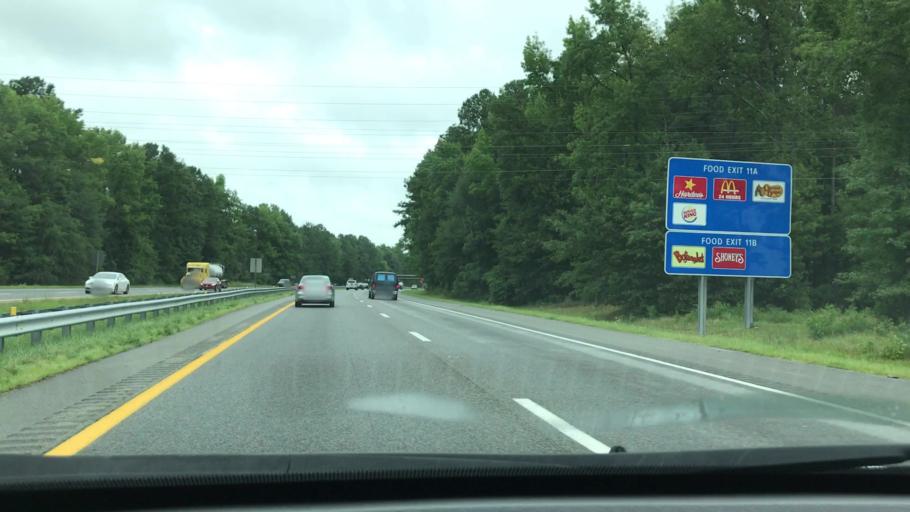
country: US
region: Virginia
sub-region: City of Emporia
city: Emporia
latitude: 36.6828
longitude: -77.5578
